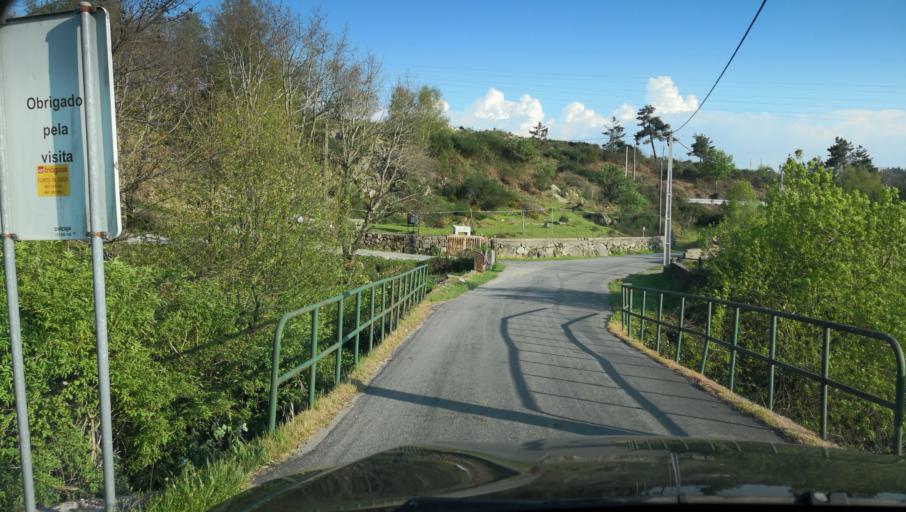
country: PT
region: Vila Real
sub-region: Santa Marta de Penaguiao
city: Santa Marta de Penaguiao
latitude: 41.2857
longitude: -7.8319
